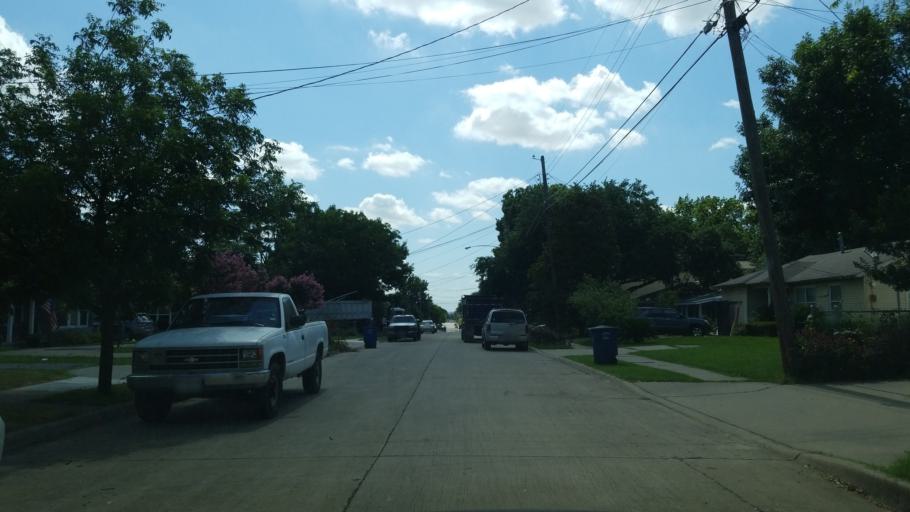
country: US
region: Texas
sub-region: Dallas County
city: University Park
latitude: 32.8877
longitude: -96.8349
